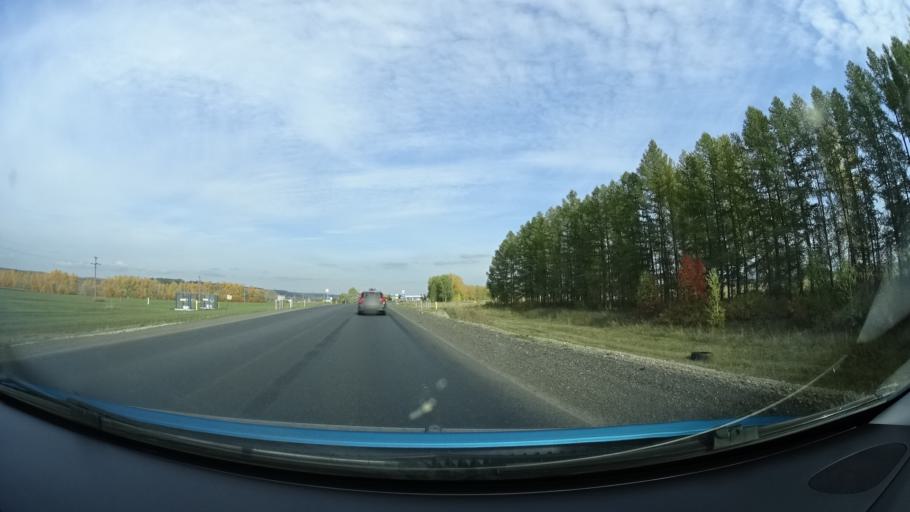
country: RU
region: Bashkortostan
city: Kandry
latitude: 54.5289
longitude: 54.0676
